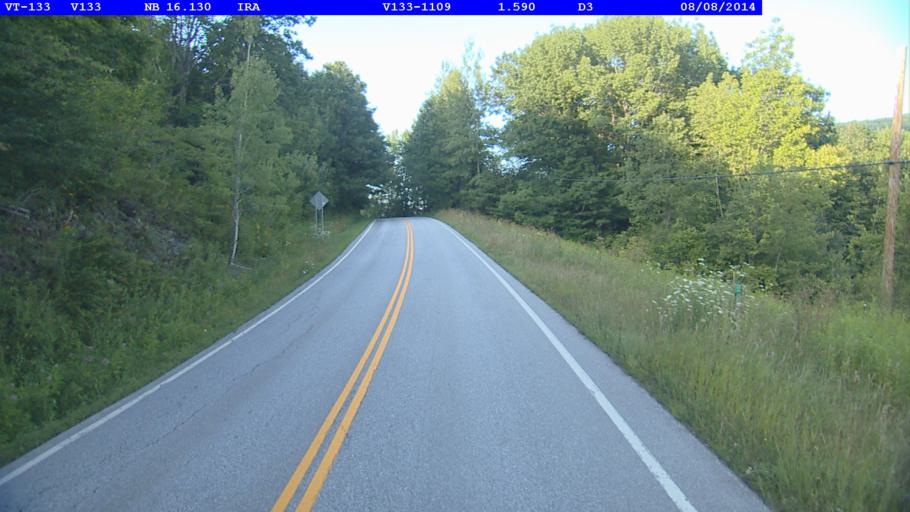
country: US
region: Vermont
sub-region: Rutland County
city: West Rutland
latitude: 43.5167
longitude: -73.0720
